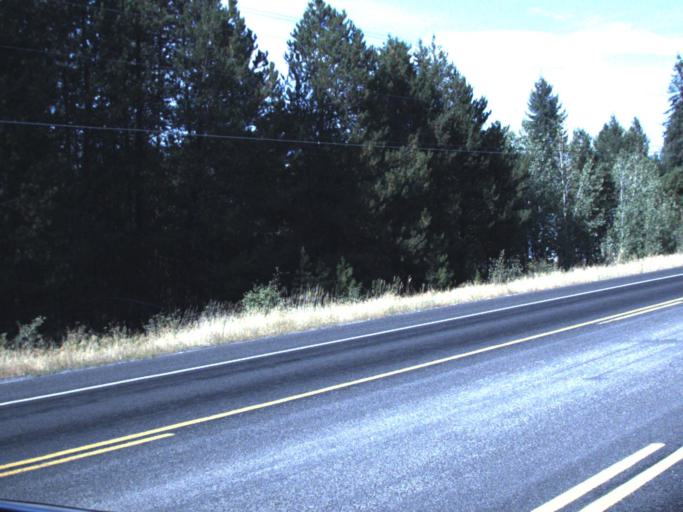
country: US
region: Washington
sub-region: Pend Oreille County
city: Newport
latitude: 48.1178
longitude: -117.2105
